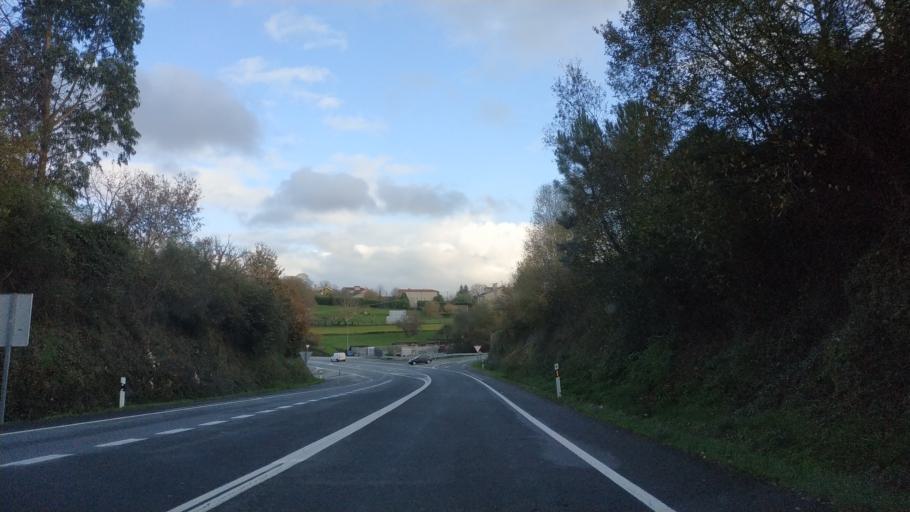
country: ES
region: Galicia
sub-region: Provincia de Pontevedra
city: Silleda
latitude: 42.7954
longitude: -8.1704
